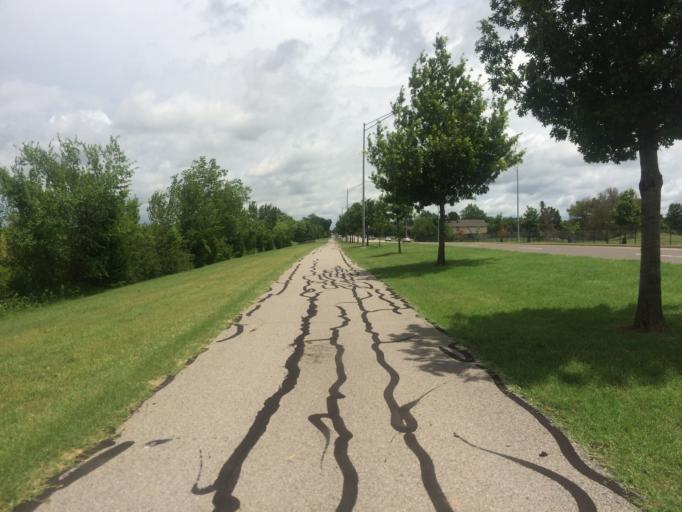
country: US
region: Oklahoma
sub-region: Cleveland County
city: Norman
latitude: 35.2331
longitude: -97.4709
